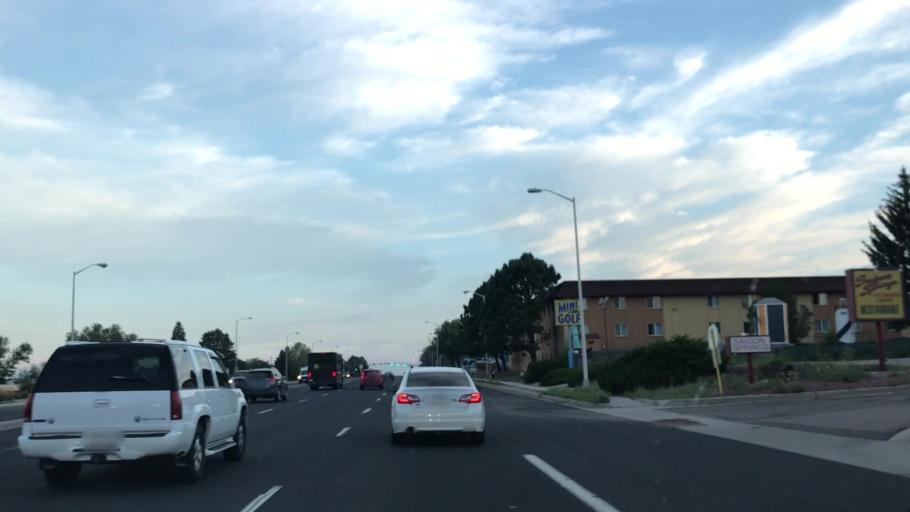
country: US
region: Colorado
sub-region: El Paso County
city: Cimarron Hills
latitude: 38.8809
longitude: -104.7571
